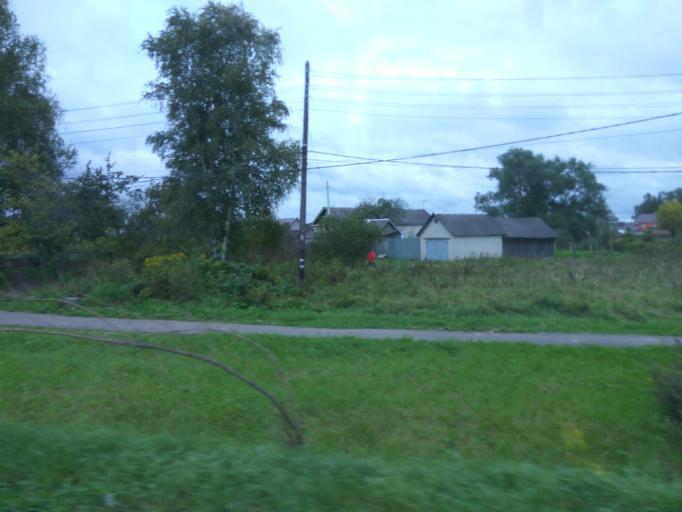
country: RU
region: Moskovskaya
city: Malyshevo
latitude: 55.4987
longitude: 38.3587
